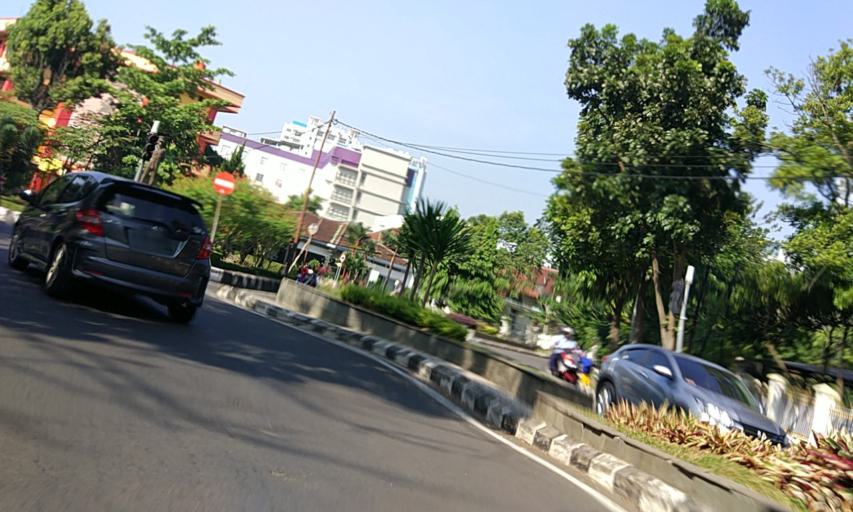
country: ID
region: West Java
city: Bandung
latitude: -6.9128
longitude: 107.6131
